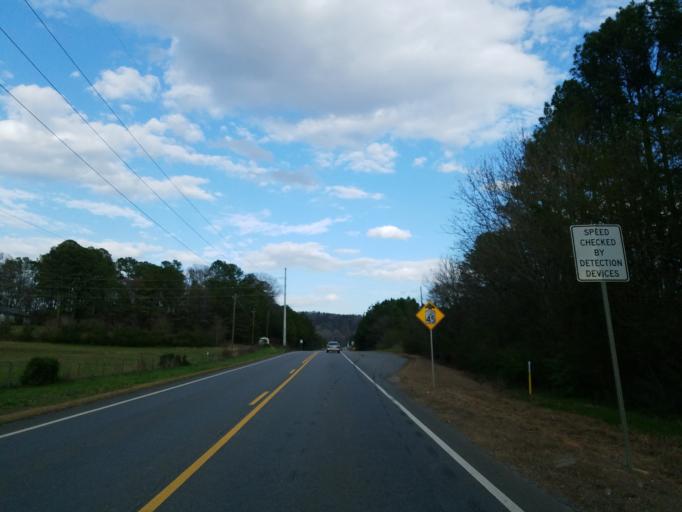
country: US
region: Georgia
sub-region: Bartow County
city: Rydal
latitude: 34.4345
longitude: -84.7078
